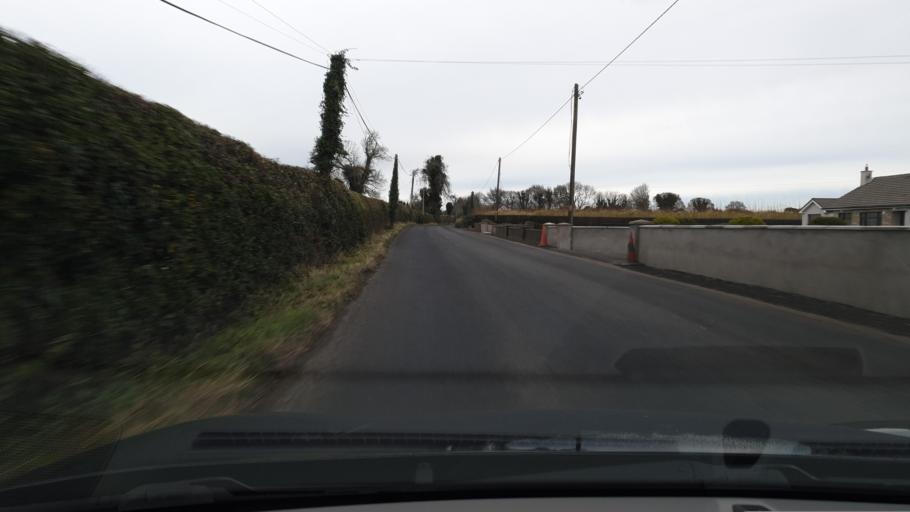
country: IE
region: Leinster
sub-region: An Mhi
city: Ashbourne
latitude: 53.5292
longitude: -6.4076
